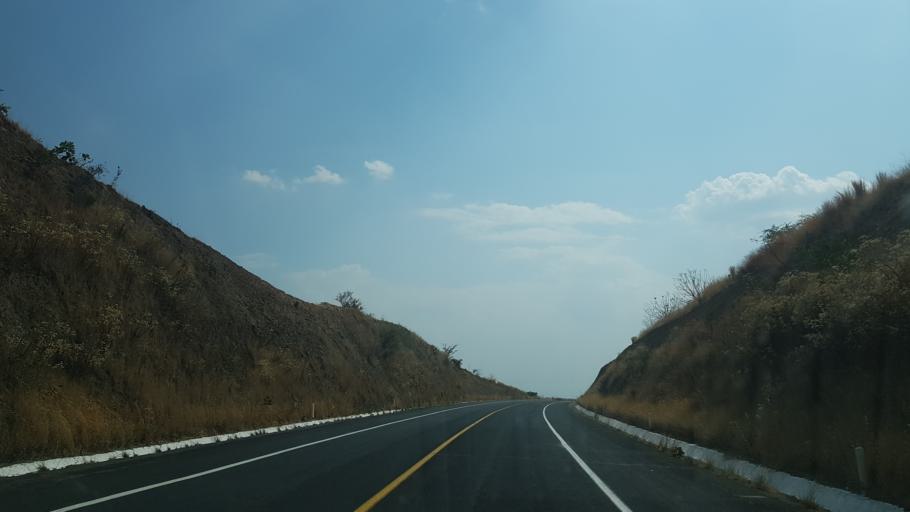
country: MX
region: Morelos
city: Tlacotepec
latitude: 18.8007
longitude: -98.7092
